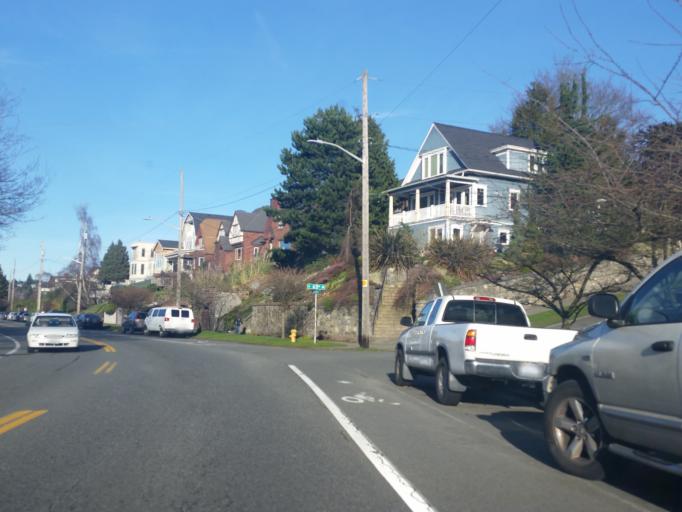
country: US
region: Washington
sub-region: King County
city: Seattle
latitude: 47.6758
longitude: -122.3328
